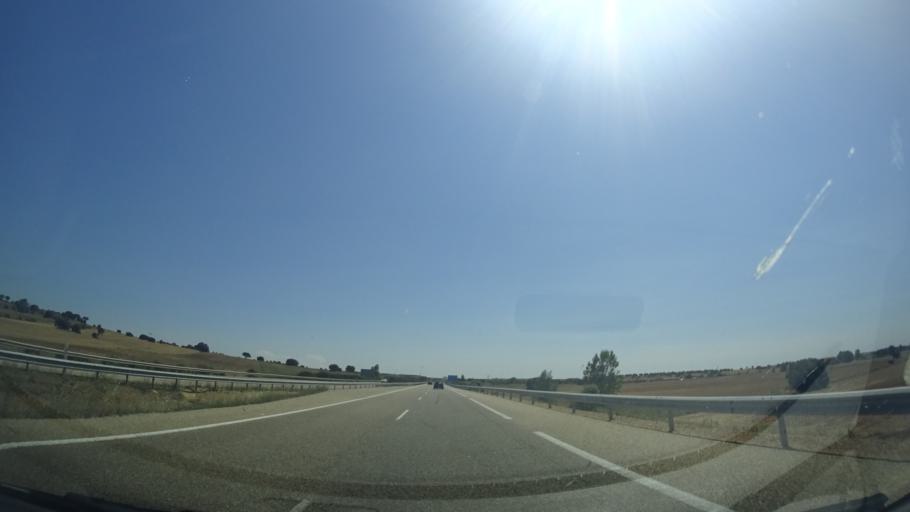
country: ES
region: Castille and Leon
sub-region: Provincia de Leon
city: Villaquejida
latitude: 42.1642
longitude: -5.6357
